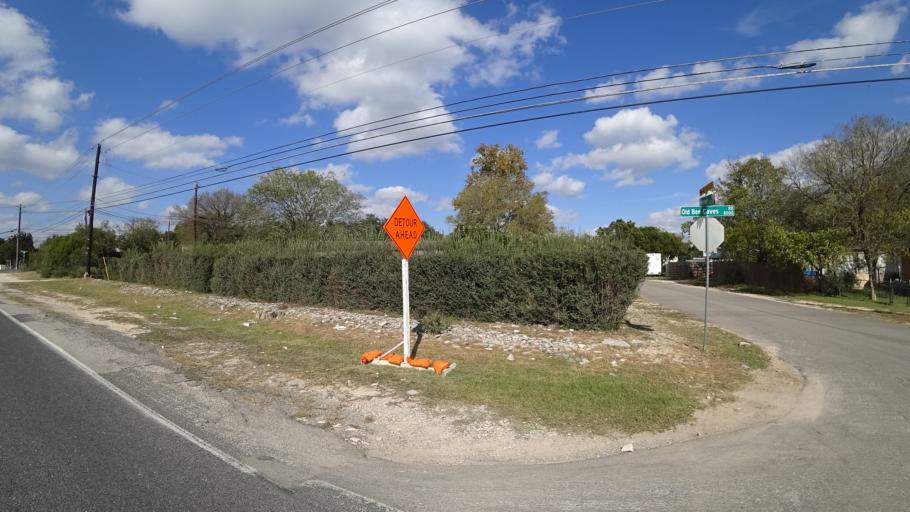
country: US
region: Texas
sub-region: Travis County
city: Barton Creek
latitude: 30.2466
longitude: -97.8824
